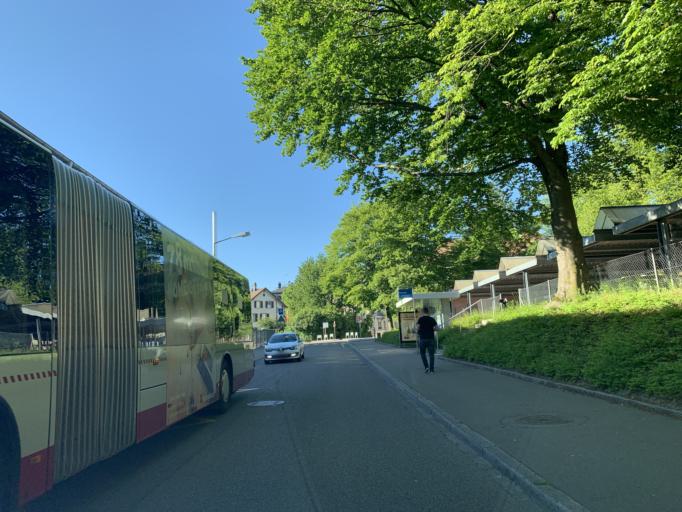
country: CH
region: Zurich
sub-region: Bezirk Winterthur
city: Toess (Kreis 4) / Eichliacker
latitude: 47.4867
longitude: 8.7085
